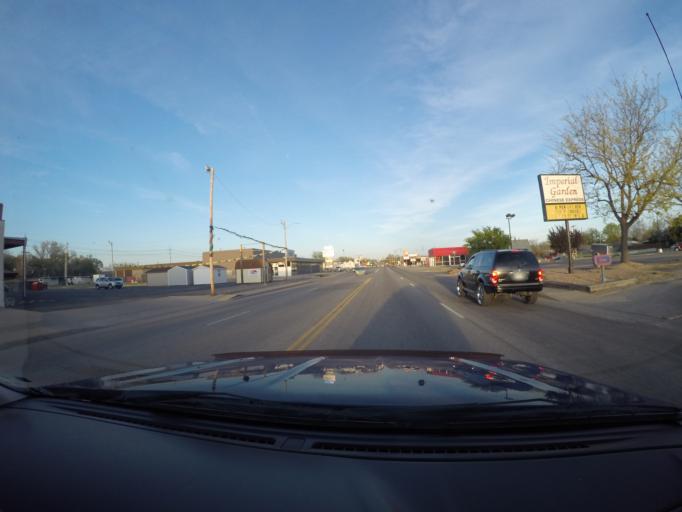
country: US
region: Kansas
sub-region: Saline County
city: Salina
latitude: 38.8271
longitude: -97.5970
